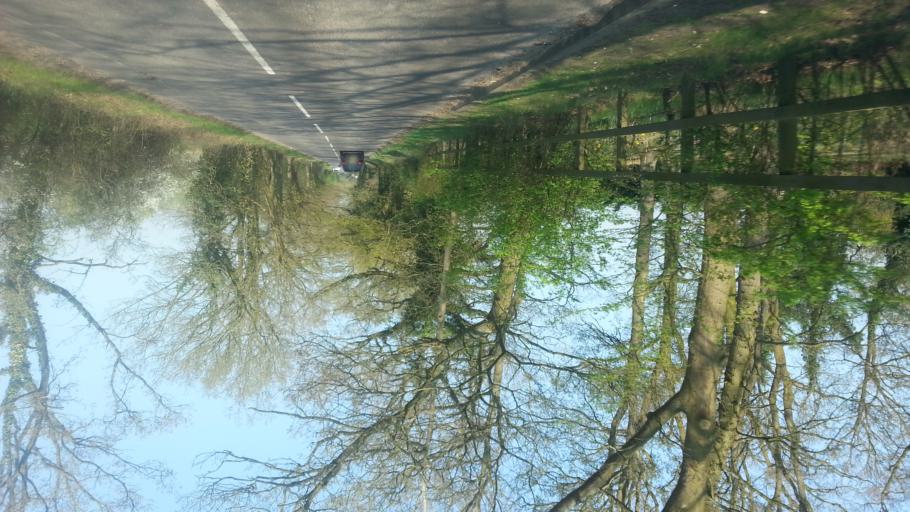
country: GB
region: England
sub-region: Suffolk
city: Thurston
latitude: 52.2412
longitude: 0.8235
